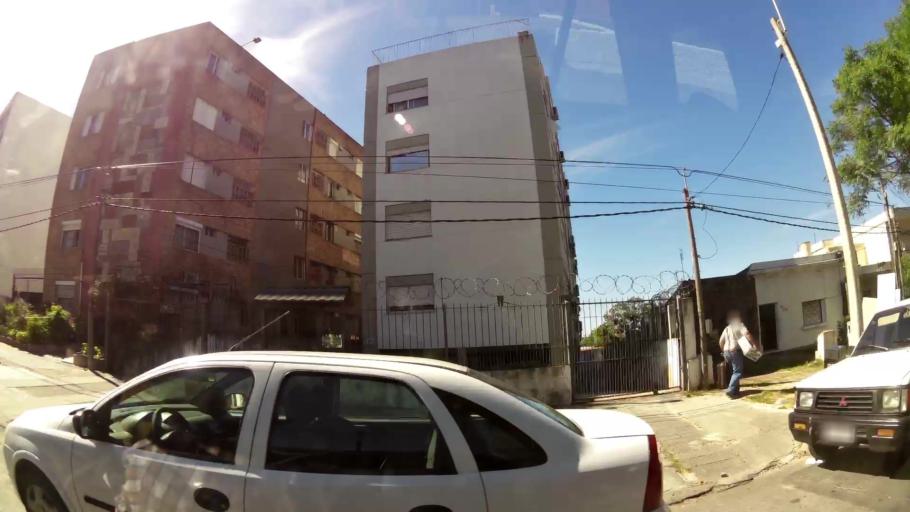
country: UY
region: Montevideo
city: Montevideo
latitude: -34.8893
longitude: -56.1254
